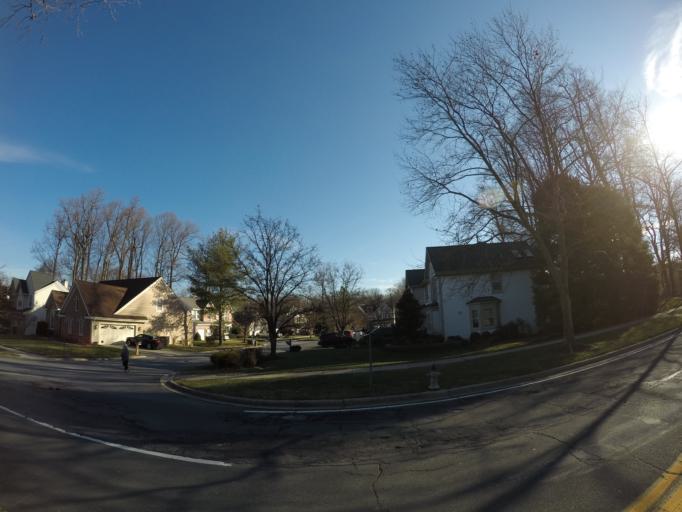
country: US
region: Maryland
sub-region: Montgomery County
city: Olney
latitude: 39.1500
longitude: -77.0497
